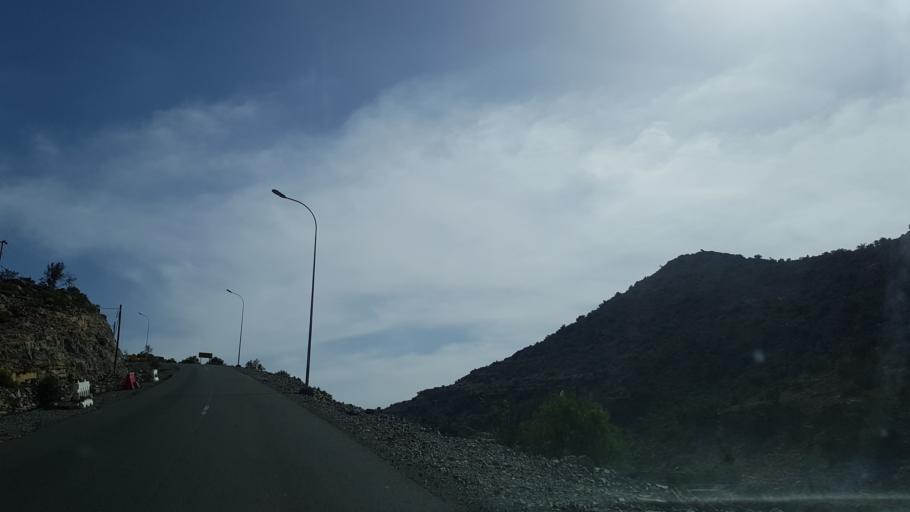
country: OM
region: Muhafazat ad Dakhiliyah
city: Izki
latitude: 23.1128
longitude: 57.6593
